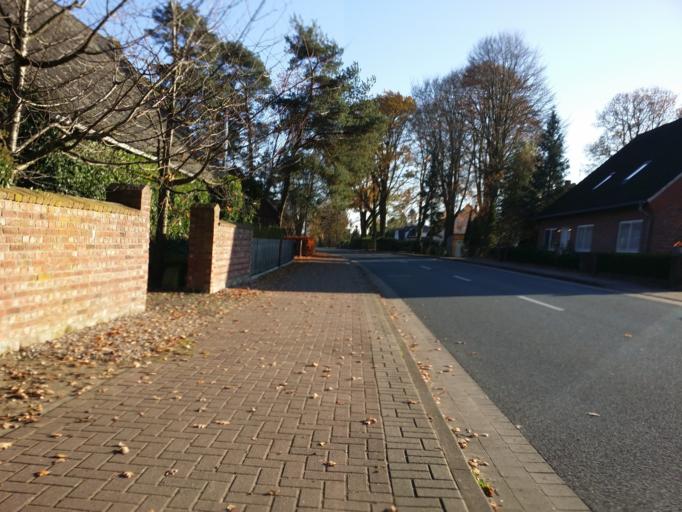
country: DE
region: Lower Saxony
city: Langwedel
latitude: 53.0310
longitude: 9.1586
